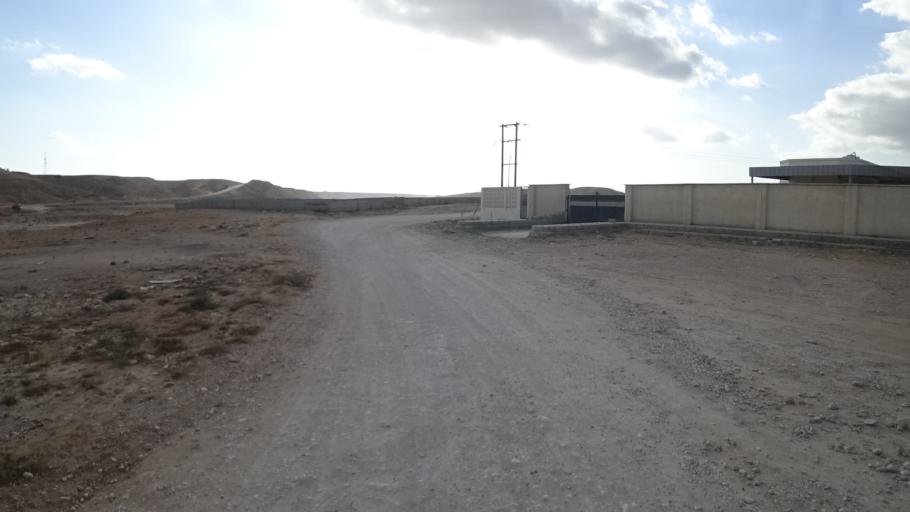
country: OM
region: Zufar
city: Salalah
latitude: 16.9601
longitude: 53.8682
